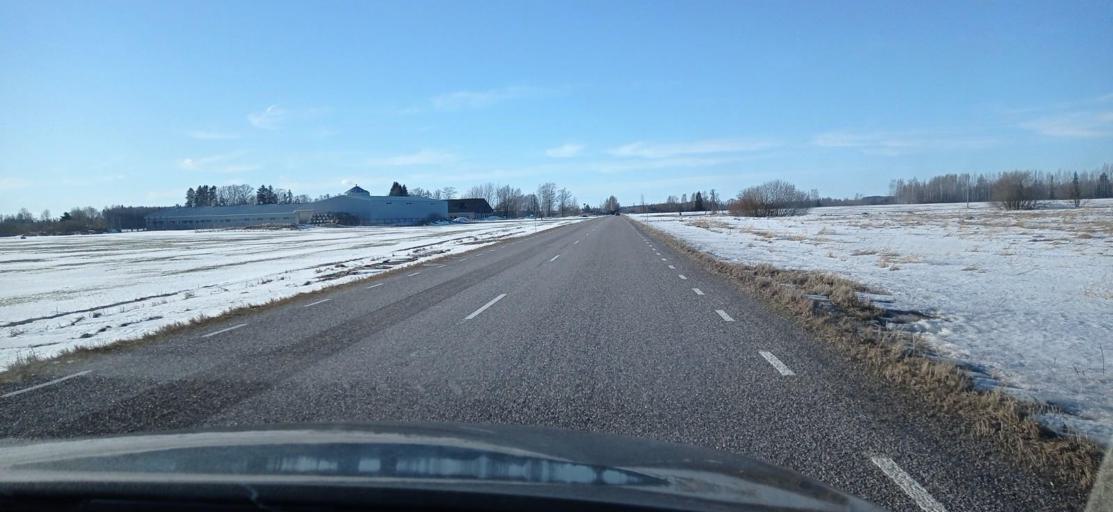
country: EE
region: Tartu
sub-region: Alatskivi vald
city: Kallaste
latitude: 58.4945
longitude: 27.2197
